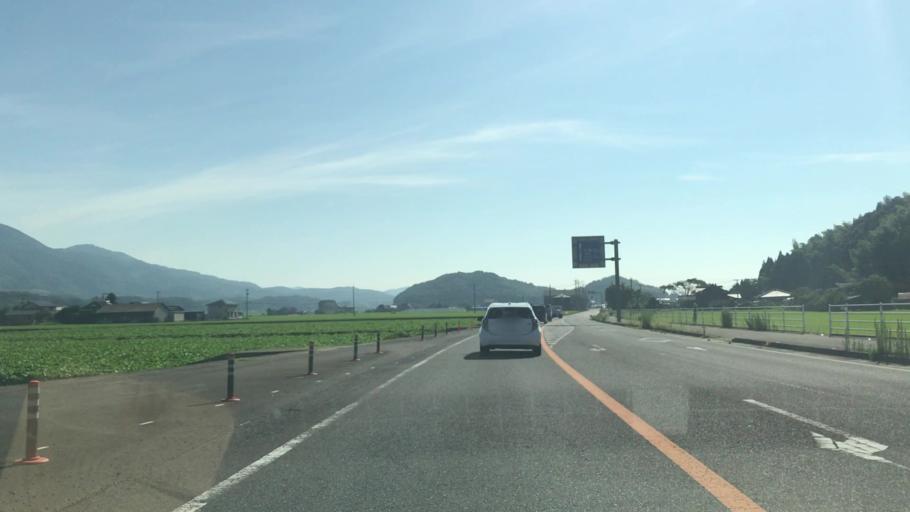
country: JP
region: Saga Prefecture
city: Takeocho-takeo
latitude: 33.2088
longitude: 130.0674
